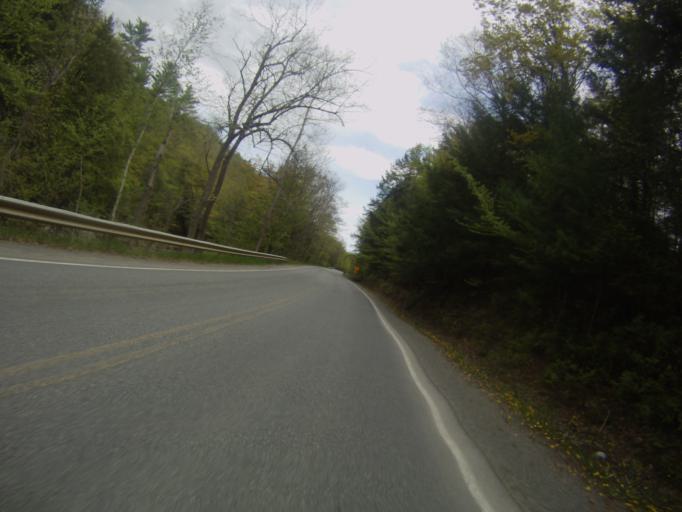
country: US
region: New York
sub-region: Essex County
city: Port Henry
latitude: 43.9461
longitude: -73.4947
